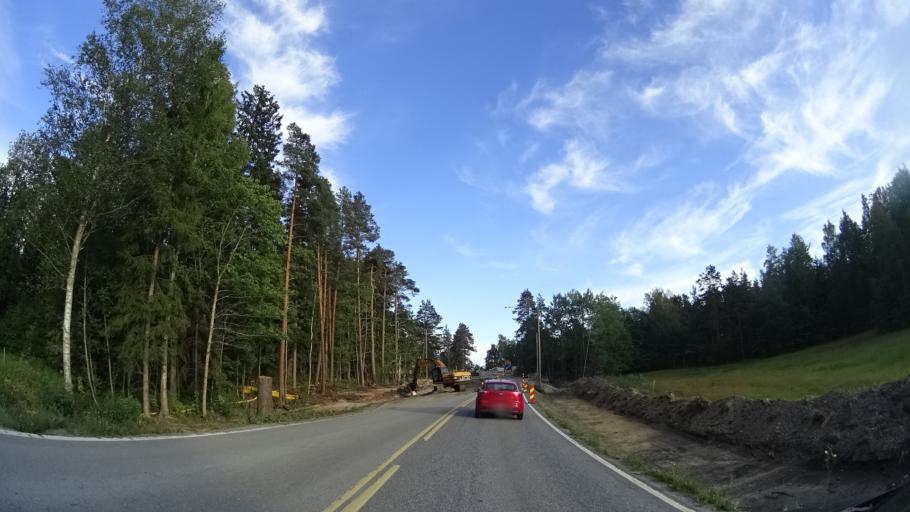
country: FI
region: Uusimaa
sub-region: Helsinki
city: Kirkkonummi
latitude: 60.2195
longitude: 24.4739
